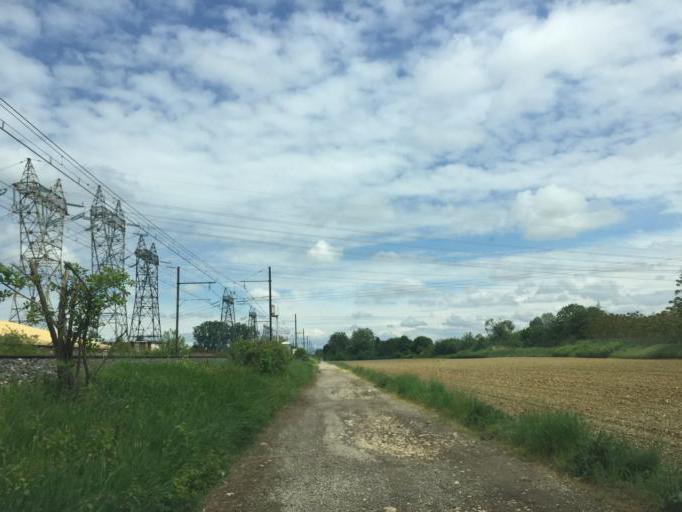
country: FR
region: Rhone-Alpes
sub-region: Departement de l'Ain
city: La Boisse
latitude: 45.8370
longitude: 5.0220
